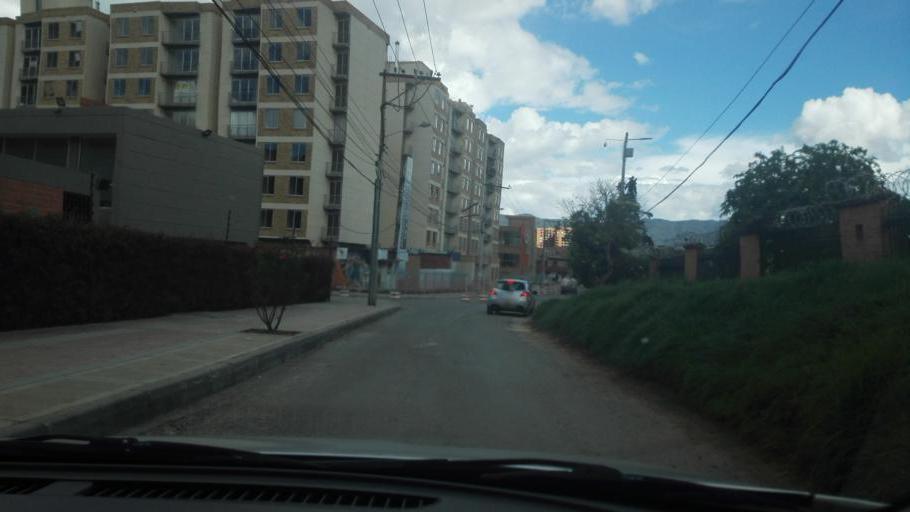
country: CO
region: Cundinamarca
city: Cota
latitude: 4.7386
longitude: -74.0707
